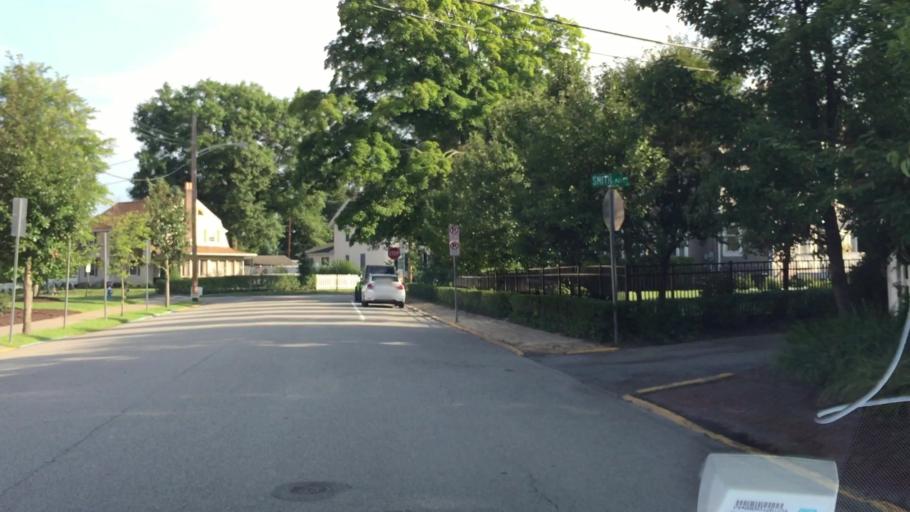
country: US
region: Pennsylvania
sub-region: Allegheny County
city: Sewickley
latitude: 40.5354
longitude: -80.1795
